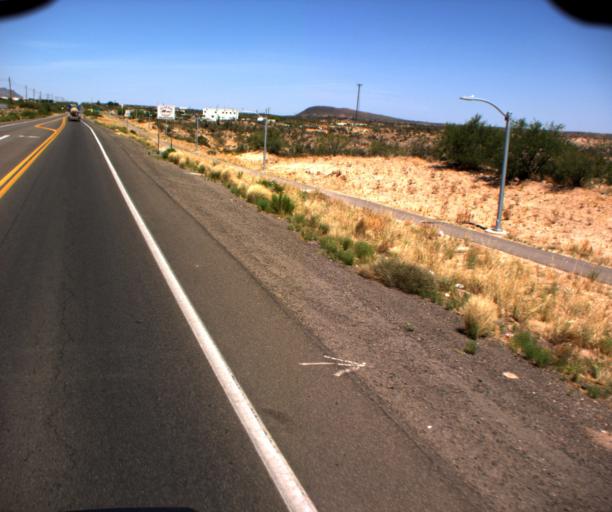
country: US
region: Arizona
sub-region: Gila County
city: Peridot
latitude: 33.2999
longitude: -110.4646
